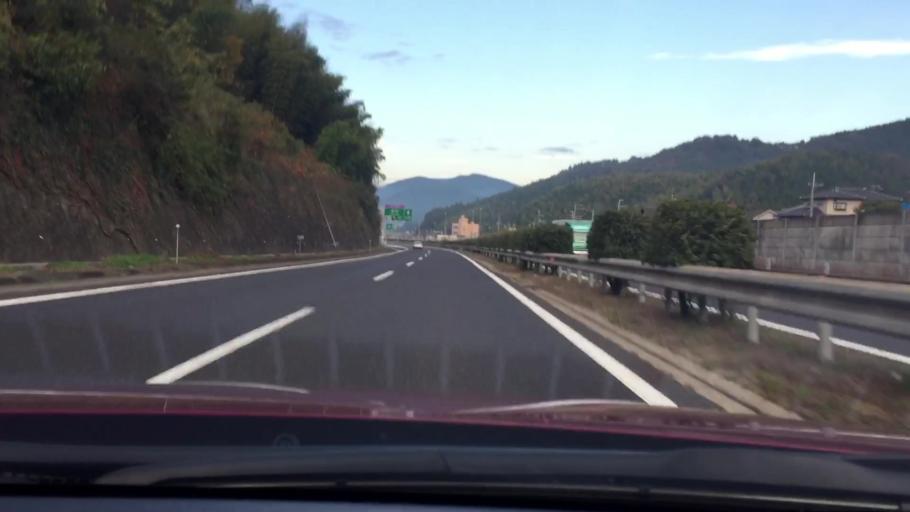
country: JP
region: Hyogo
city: Himeji
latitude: 34.9618
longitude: 134.6966
